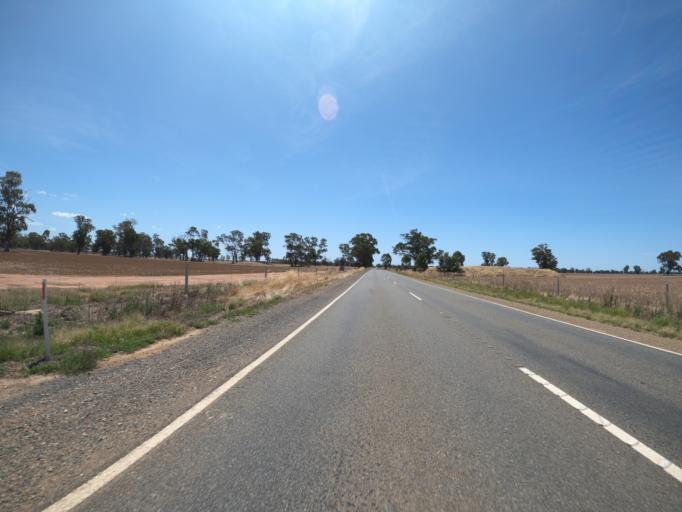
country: AU
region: Victoria
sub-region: Moira
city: Yarrawonga
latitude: -36.1712
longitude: 145.9672
